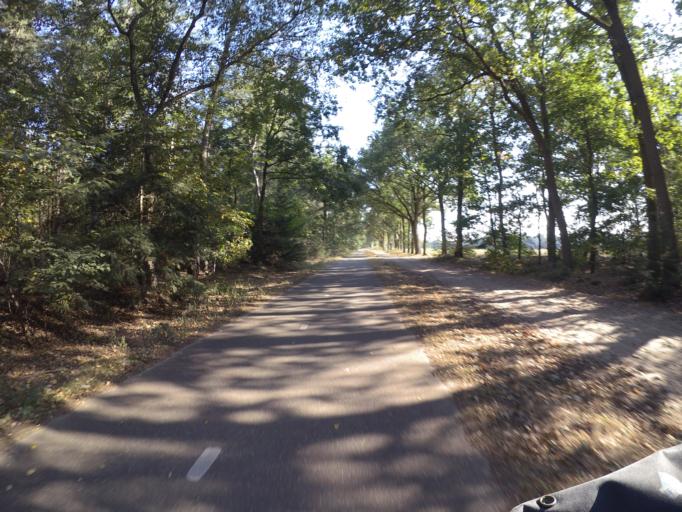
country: NL
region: North Brabant
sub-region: Gemeente Oirschot
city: Oostelbeers
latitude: 51.4739
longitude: 5.2860
